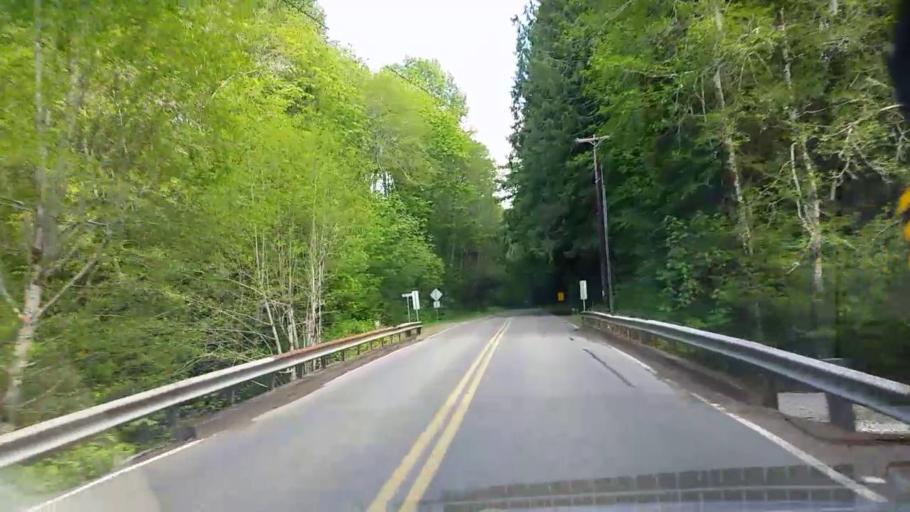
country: US
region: Washington
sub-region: Mason County
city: Shelton
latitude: 47.3158
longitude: -123.2554
